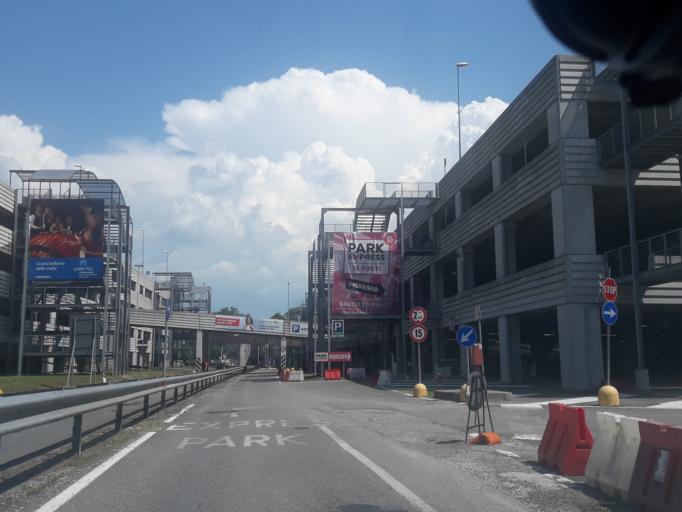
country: IT
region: Friuli Venezia Giulia
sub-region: Provincia di Udine
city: Passons
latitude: 46.0874
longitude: 13.1800
